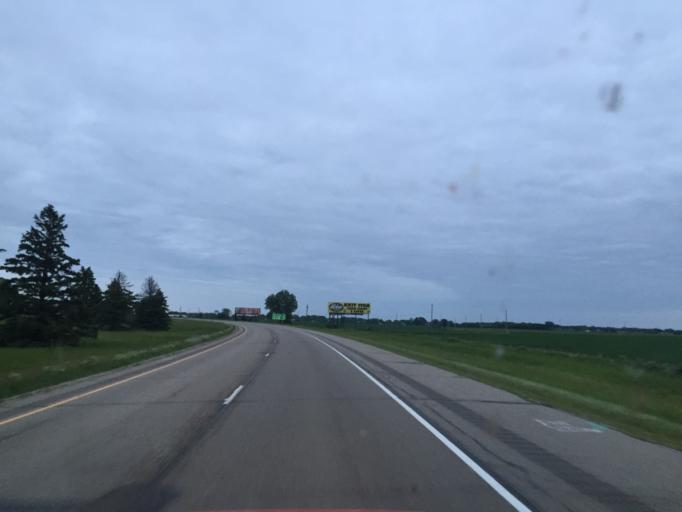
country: US
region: Minnesota
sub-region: Mower County
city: Austin
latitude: 43.6597
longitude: -93.0314
